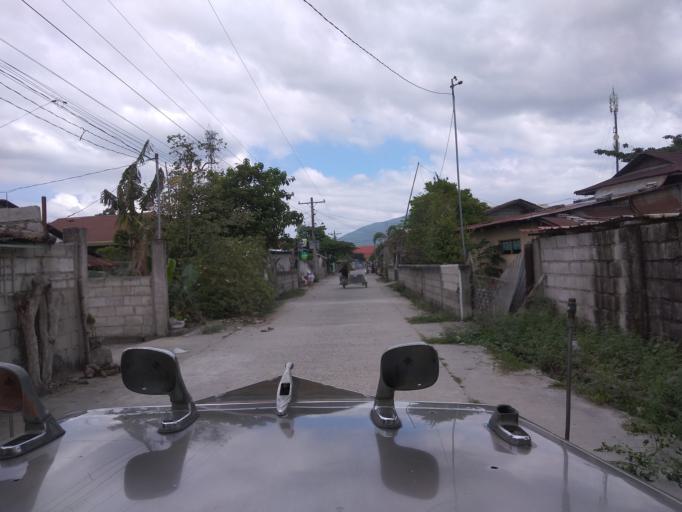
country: PH
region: Central Luzon
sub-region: Province of Pampanga
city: Malino
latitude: 15.1167
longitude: 120.6976
